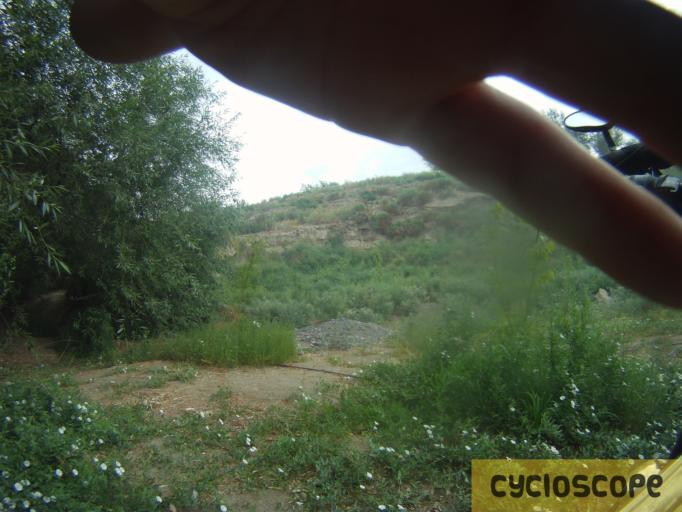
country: CN
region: Xinjiang Uygur Zizhiqu
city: Laochenglu
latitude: 42.9468
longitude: 89.0715
